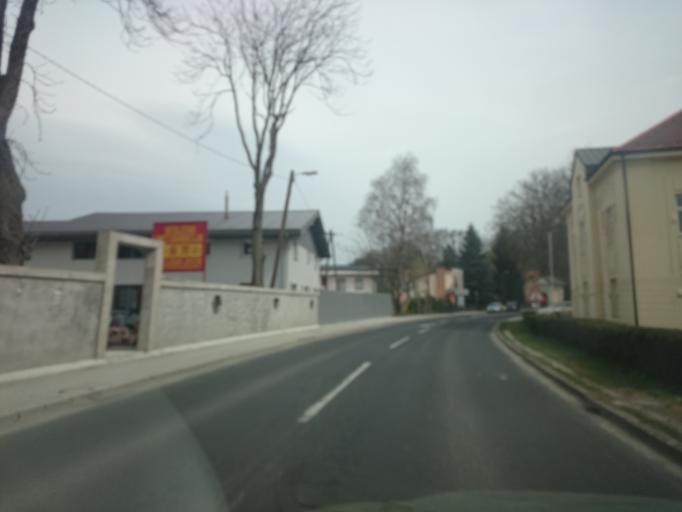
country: SI
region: Celje
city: Celje
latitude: 46.2314
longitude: 15.2762
